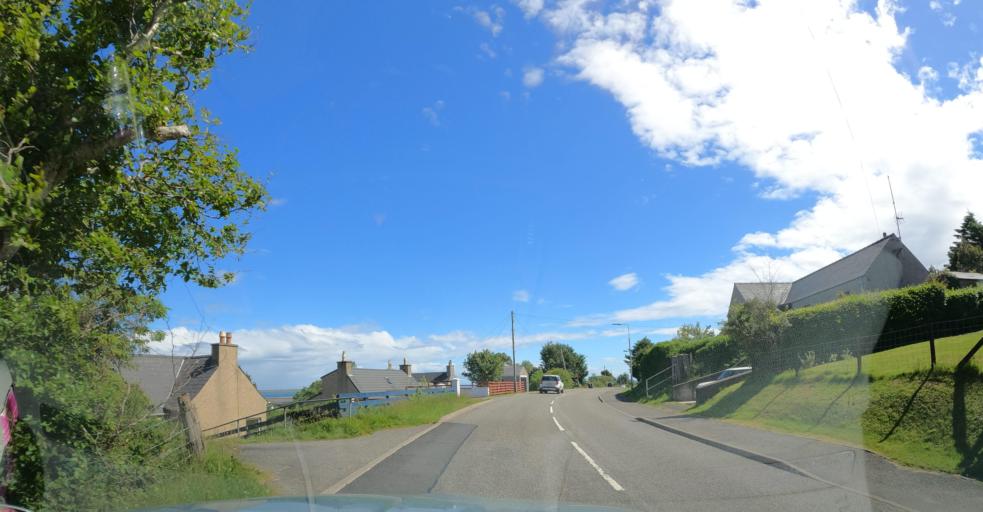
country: GB
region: Scotland
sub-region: Eilean Siar
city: Isle of Lewis
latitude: 58.2450
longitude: -6.3922
